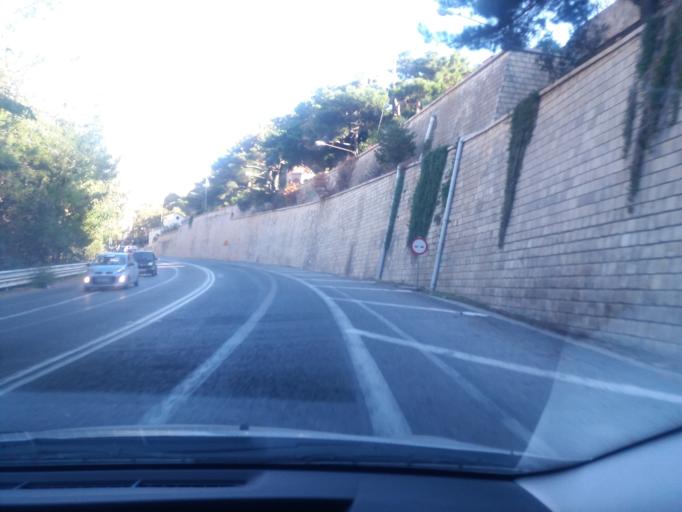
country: GR
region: Crete
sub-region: Nomos Lasithiou
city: Sision
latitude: 35.2850
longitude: 25.5398
